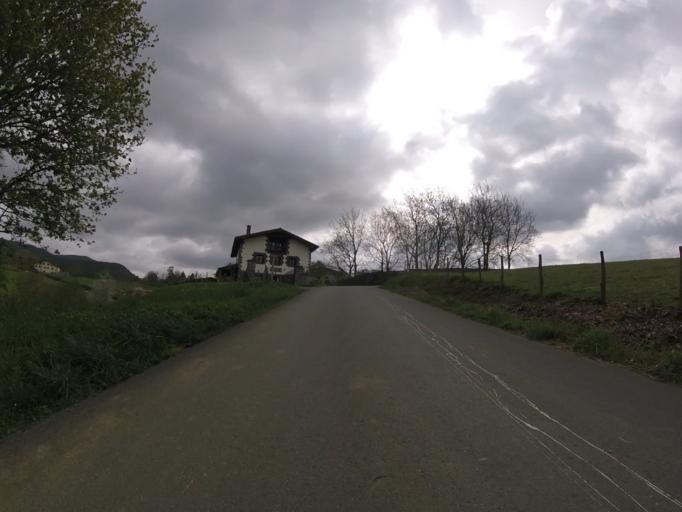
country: ES
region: Basque Country
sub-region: Provincia de Guipuzcoa
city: Zizurkil
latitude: 43.2057
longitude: -2.0767
